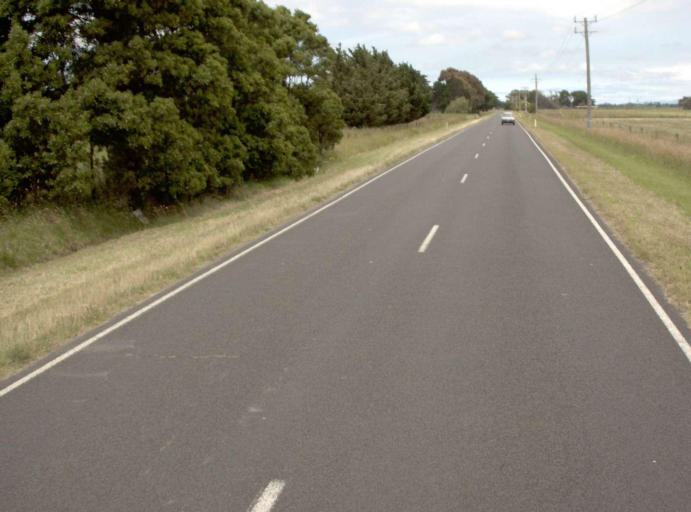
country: AU
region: Victoria
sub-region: Latrobe
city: Traralgon
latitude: -38.5457
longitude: 146.6556
